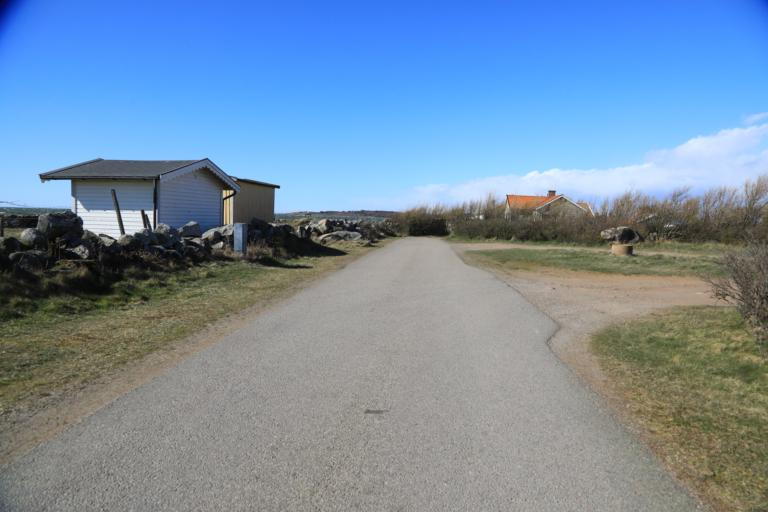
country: SE
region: Halland
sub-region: Varbergs Kommun
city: Traslovslage
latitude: 57.0682
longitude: 12.2539
